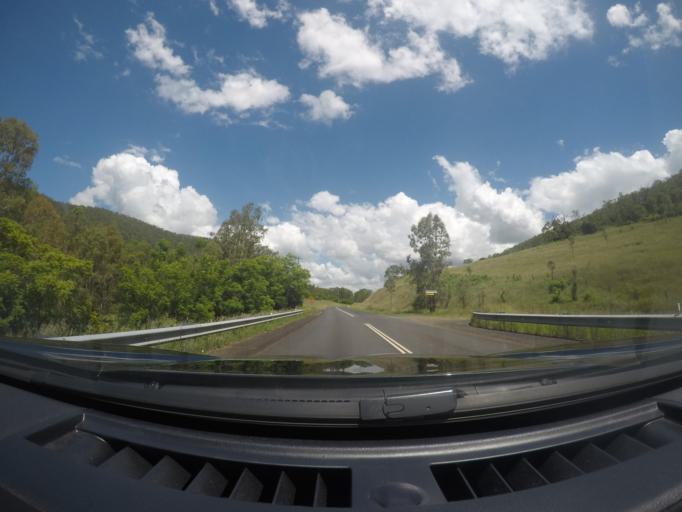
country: AU
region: Queensland
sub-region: Moreton Bay
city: Woodford
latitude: -27.1267
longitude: 152.5514
